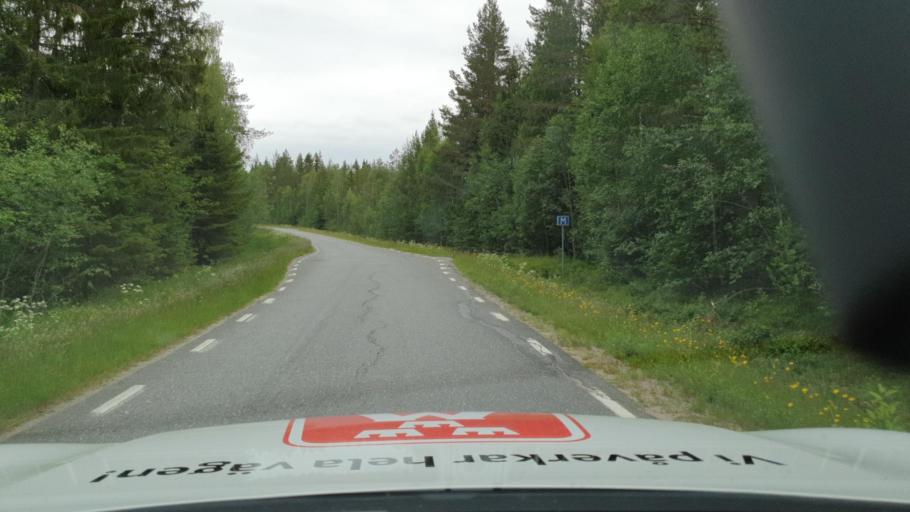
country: SE
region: Vaesterbotten
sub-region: Nordmalings Kommun
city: Nordmaling
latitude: 63.4796
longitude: 19.4577
